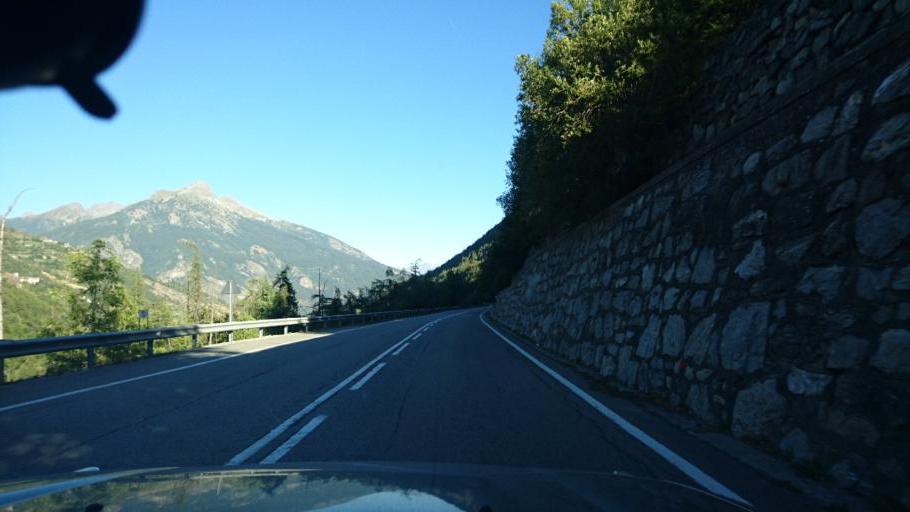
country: IT
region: Aosta Valley
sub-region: Valle d'Aosta
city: Allein
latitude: 45.8070
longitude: 7.2515
